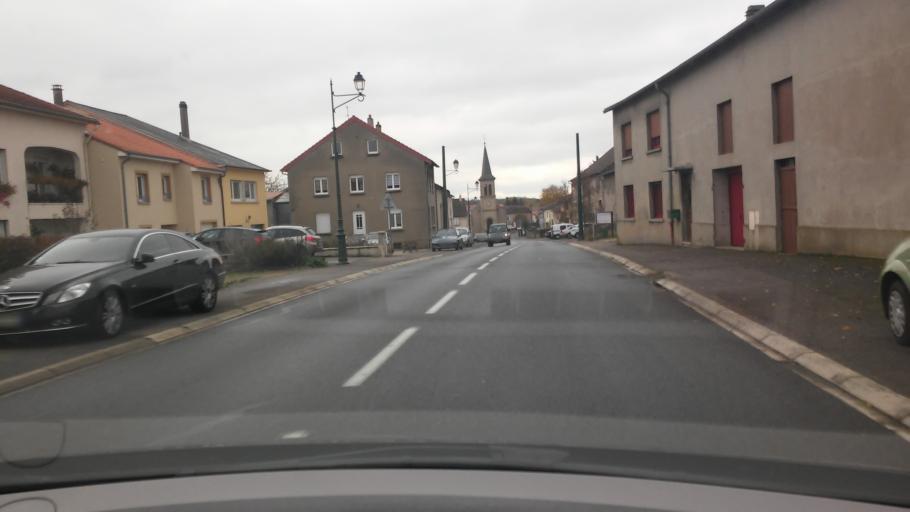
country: FR
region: Lorraine
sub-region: Departement de la Moselle
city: Rurange-les-Thionville
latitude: 49.2789
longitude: 6.2298
